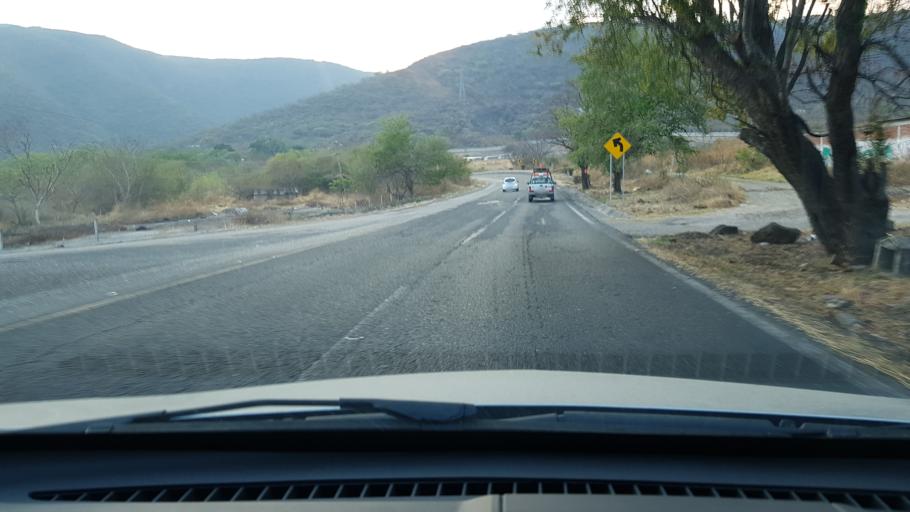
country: MX
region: Morelos
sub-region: Jiutepec
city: Independencia
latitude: 18.8589
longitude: -99.1027
